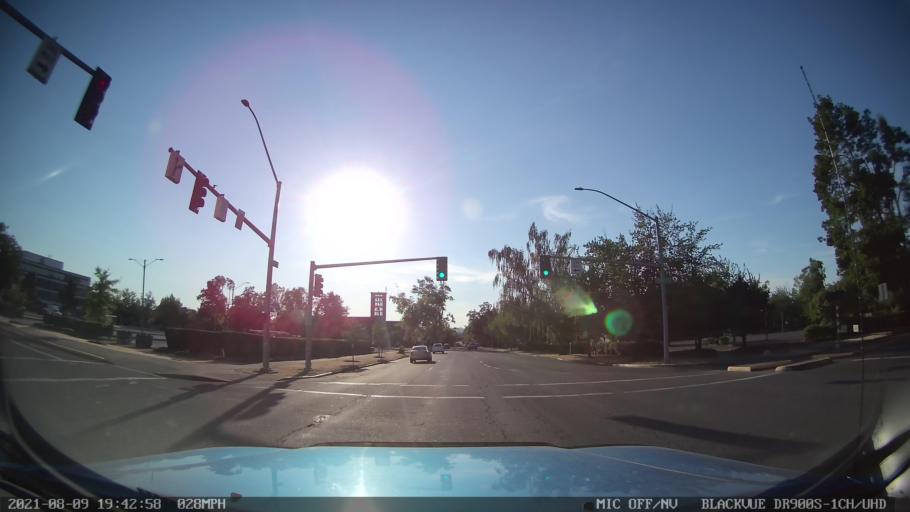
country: US
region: Oregon
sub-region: Marion County
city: Salem
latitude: 44.9423
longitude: -123.0283
